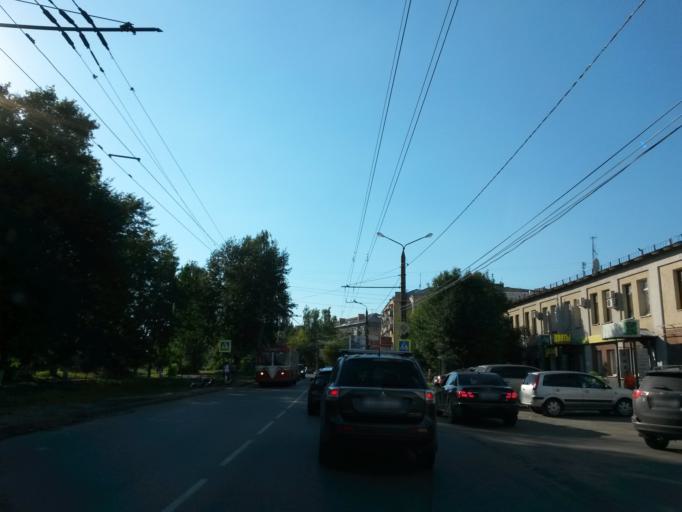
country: RU
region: Ivanovo
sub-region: Gorod Ivanovo
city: Ivanovo
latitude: 56.9970
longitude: 40.9587
